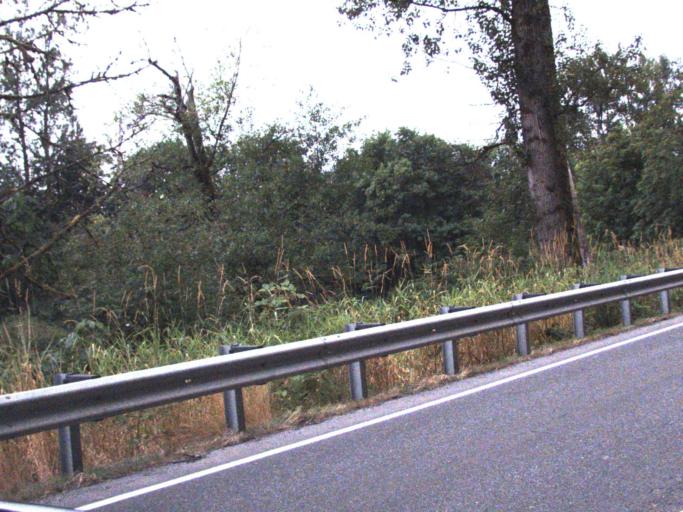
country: US
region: Washington
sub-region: King County
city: Lake Marcel-Stillwater
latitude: 47.6917
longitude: -121.9589
